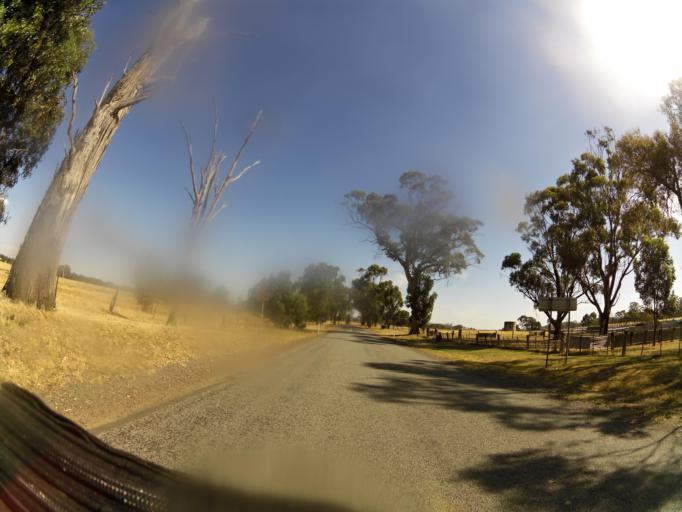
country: AU
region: Victoria
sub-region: Campaspe
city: Kyabram
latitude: -36.8944
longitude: 145.1068
